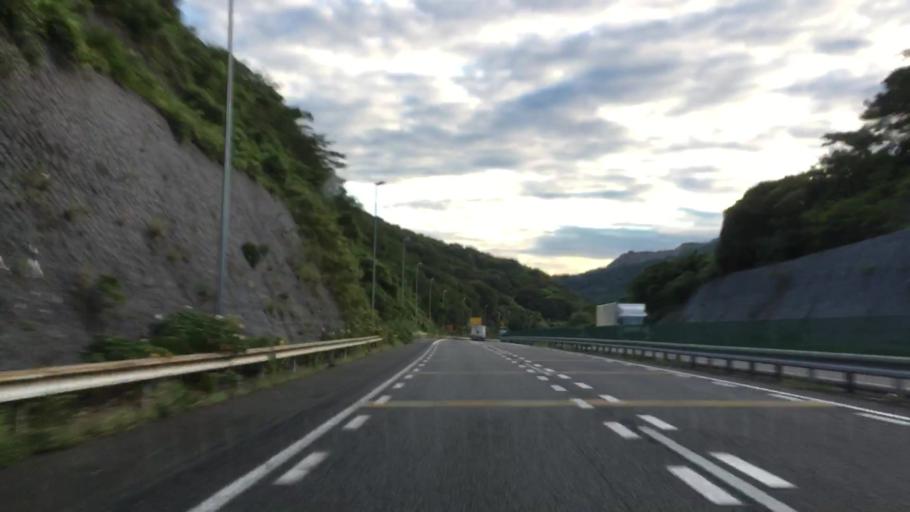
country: JP
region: Yamaguchi
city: Shimonoseki
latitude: 34.0385
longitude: 130.9696
